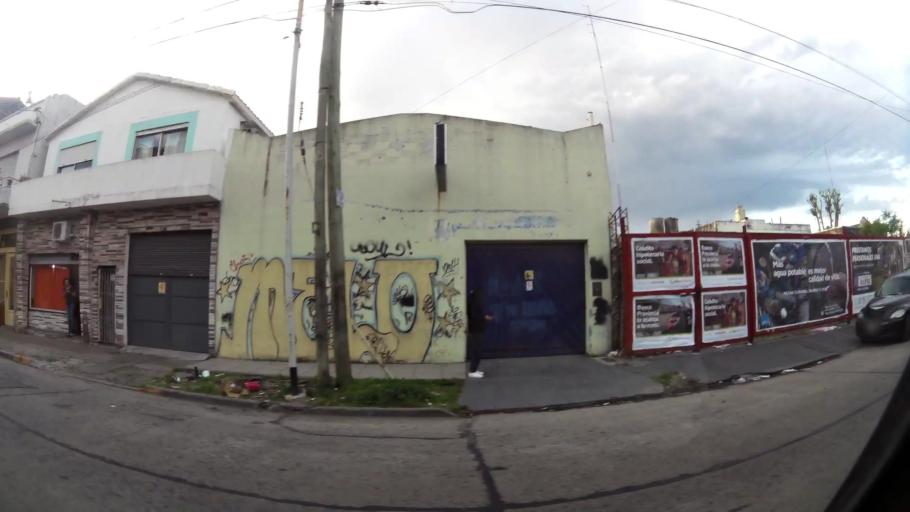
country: AR
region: Buenos Aires
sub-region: Partido de Avellaneda
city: Avellaneda
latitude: -34.6975
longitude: -58.3267
